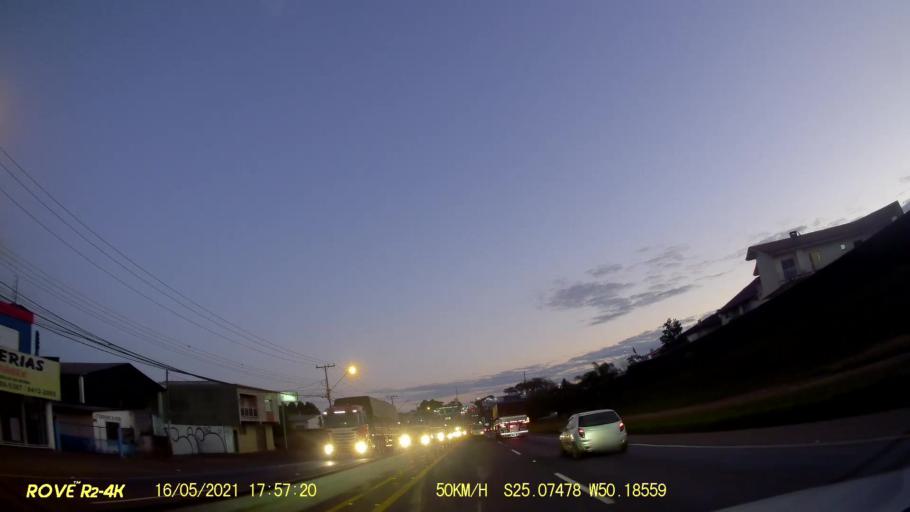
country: BR
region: Parana
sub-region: Ponta Grossa
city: Ponta Grossa
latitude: -25.0748
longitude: -50.1856
